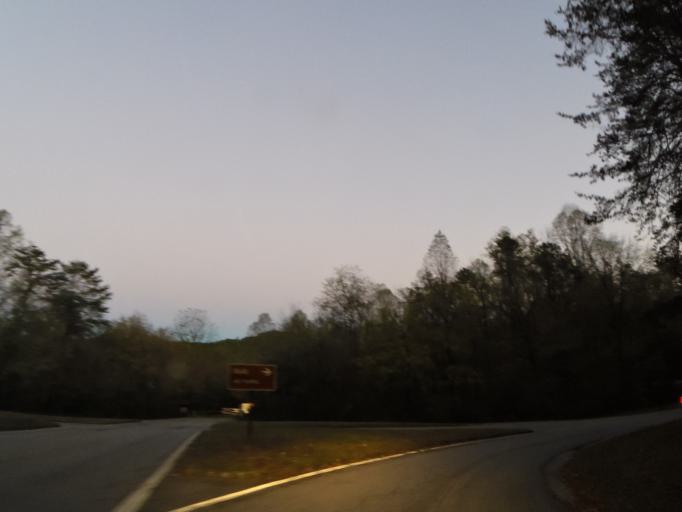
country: US
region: Tennessee
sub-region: Blount County
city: Wildwood
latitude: 35.7184
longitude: -83.8222
